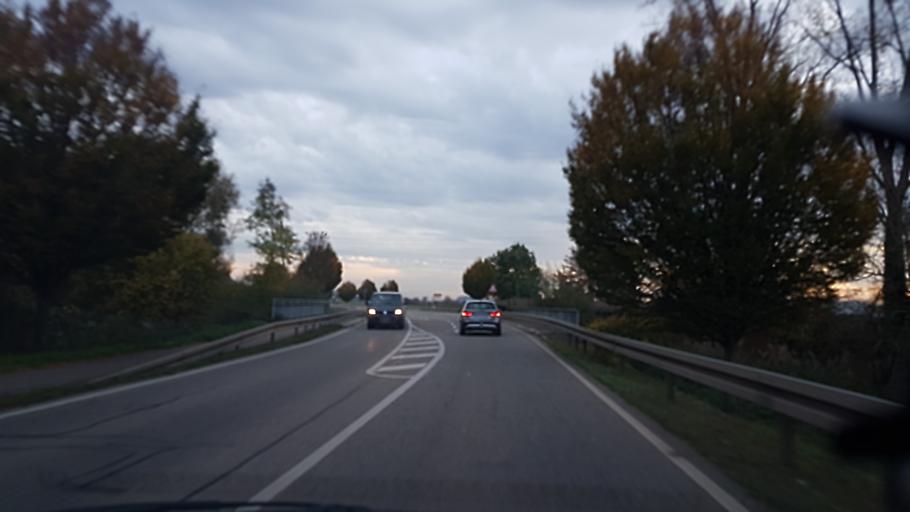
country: DE
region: Baden-Wuerttemberg
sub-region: Freiburg Region
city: Kenzingen
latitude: 48.1952
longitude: 7.7590
